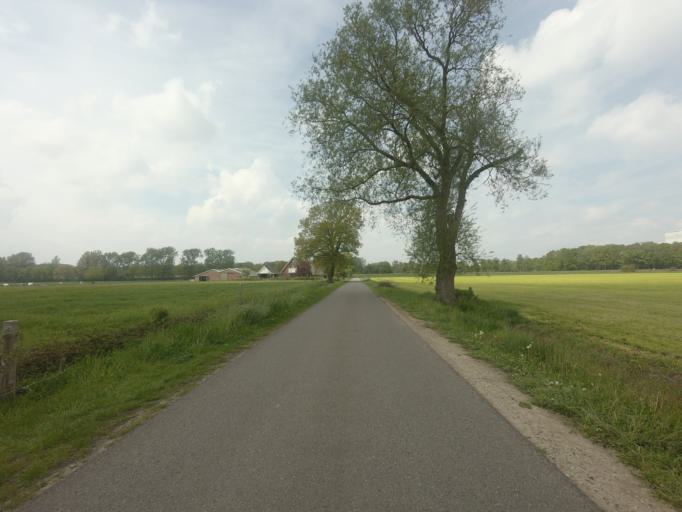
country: NL
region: Overijssel
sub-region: Gemeente Hof van Twente
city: Delden
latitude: 52.2487
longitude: 6.6907
